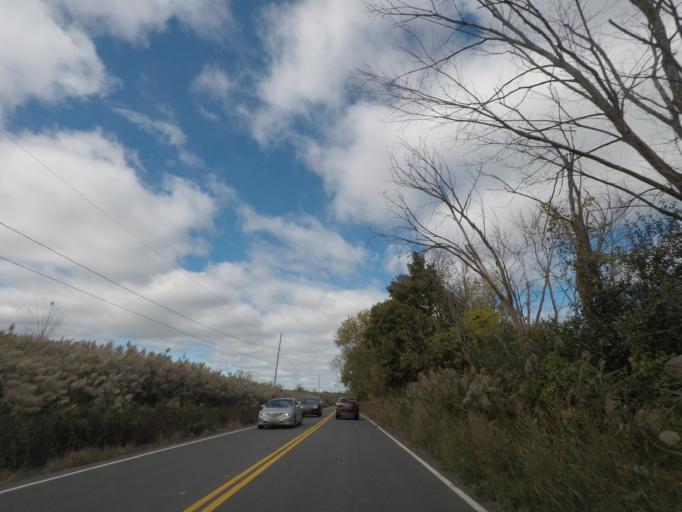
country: US
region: New York
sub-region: Albany County
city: Cohoes
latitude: 42.8132
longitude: -73.7268
